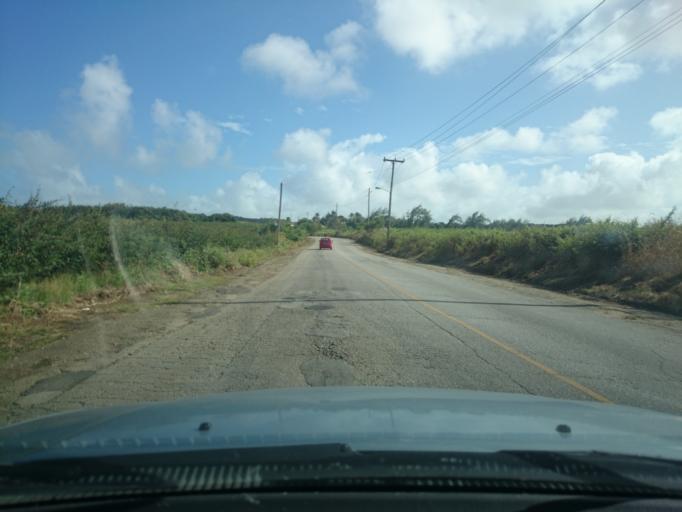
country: BB
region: Saint Lucy
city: Checker Hall
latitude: 13.2720
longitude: -59.6031
